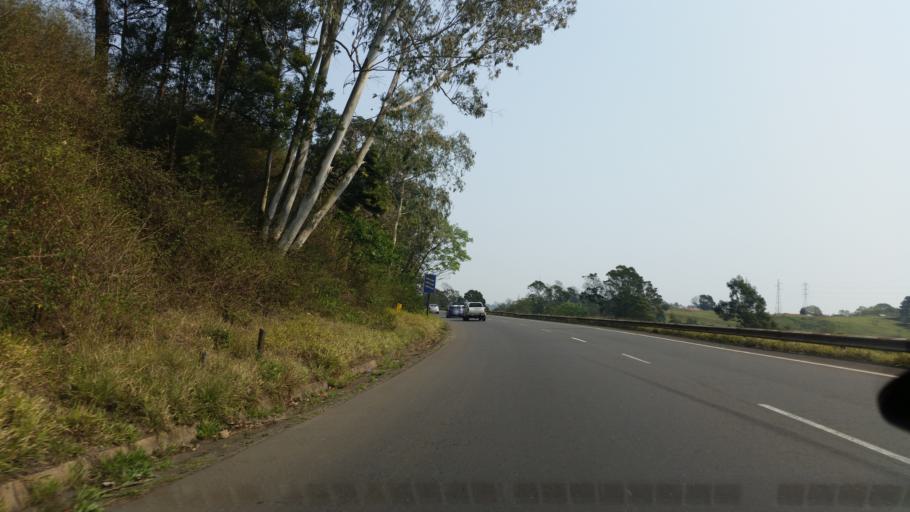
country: ZA
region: KwaZulu-Natal
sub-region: eThekwini Metropolitan Municipality
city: Mpumalanga
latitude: -29.7956
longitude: 30.7489
